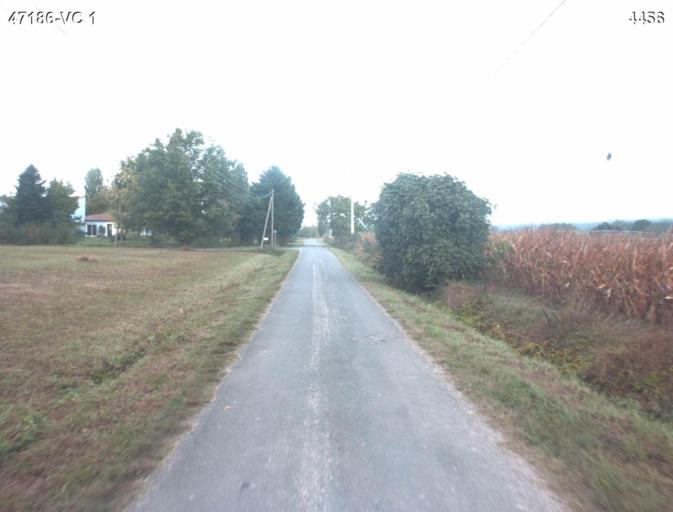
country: FR
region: Aquitaine
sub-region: Departement du Lot-et-Garonne
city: Port-Sainte-Marie
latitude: 44.2248
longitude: 0.4402
